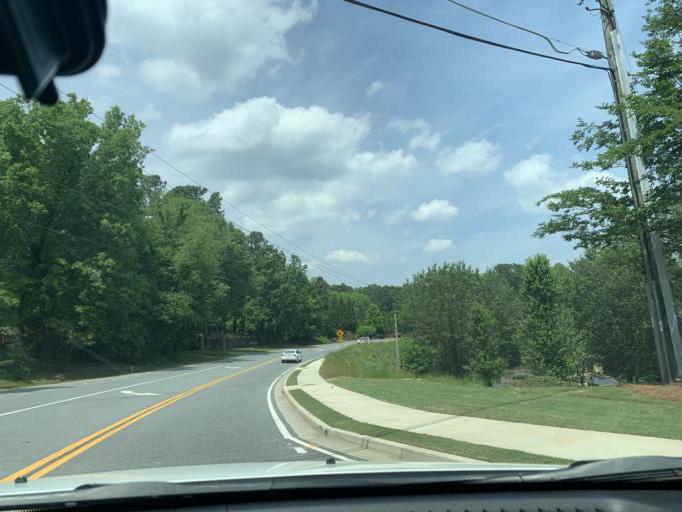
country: US
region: Georgia
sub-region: Forsyth County
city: Cumming
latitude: 34.1208
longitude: -84.1557
